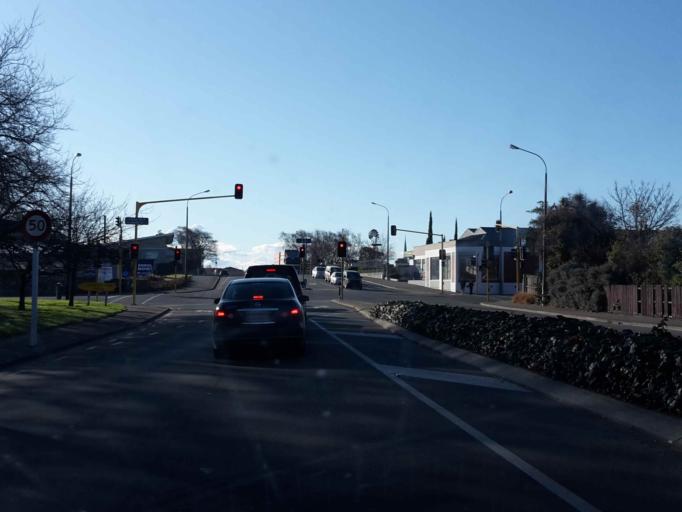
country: NZ
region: Canterbury
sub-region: Timaru District
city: Timaru
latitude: -44.4012
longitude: 171.2484
